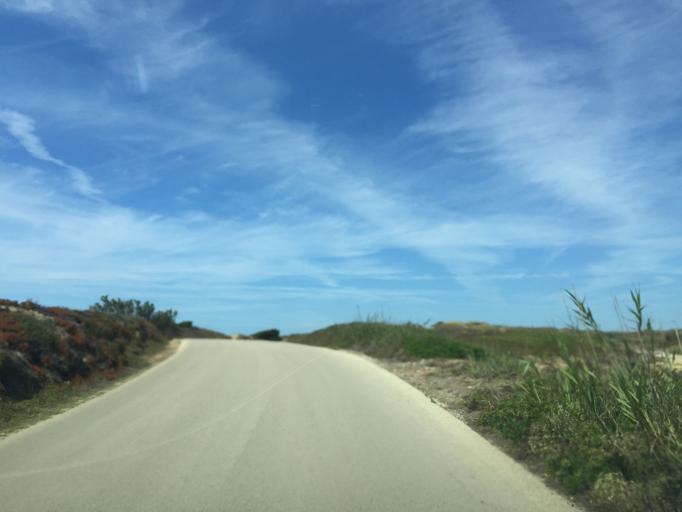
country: PT
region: Lisbon
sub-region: Lourinha
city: Lourinha
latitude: 39.1817
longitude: -9.3548
